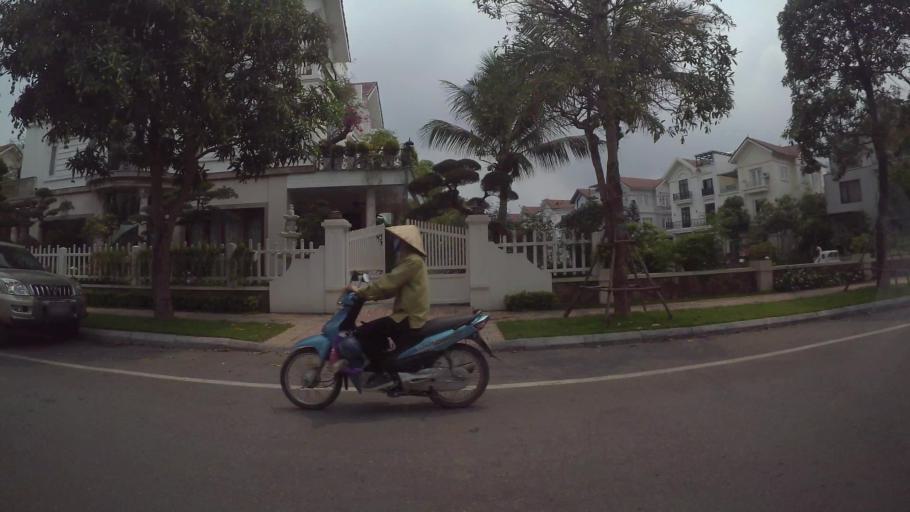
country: VN
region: Ha Noi
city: Trau Quy
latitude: 21.0428
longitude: 105.9157
